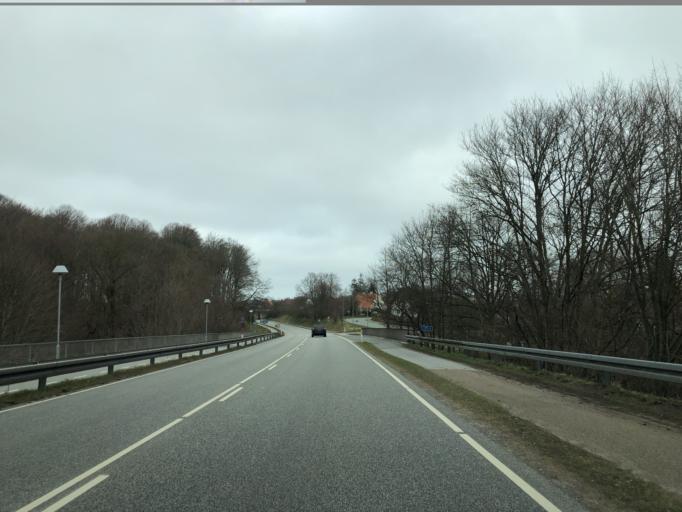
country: DK
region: North Denmark
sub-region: Frederikshavn Kommune
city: Saeby
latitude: 57.3351
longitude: 10.5111
